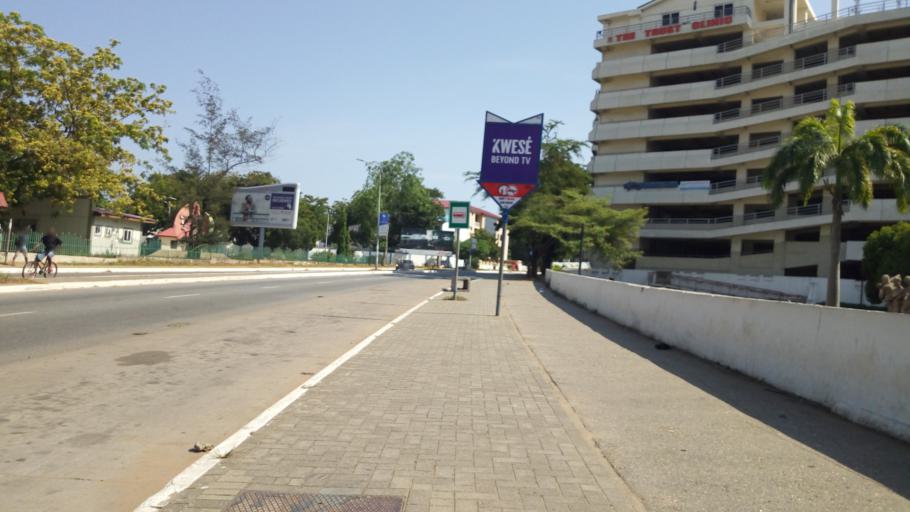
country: GH
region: Greater Accra
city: Accra
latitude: 5.5539
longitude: -0.1999
